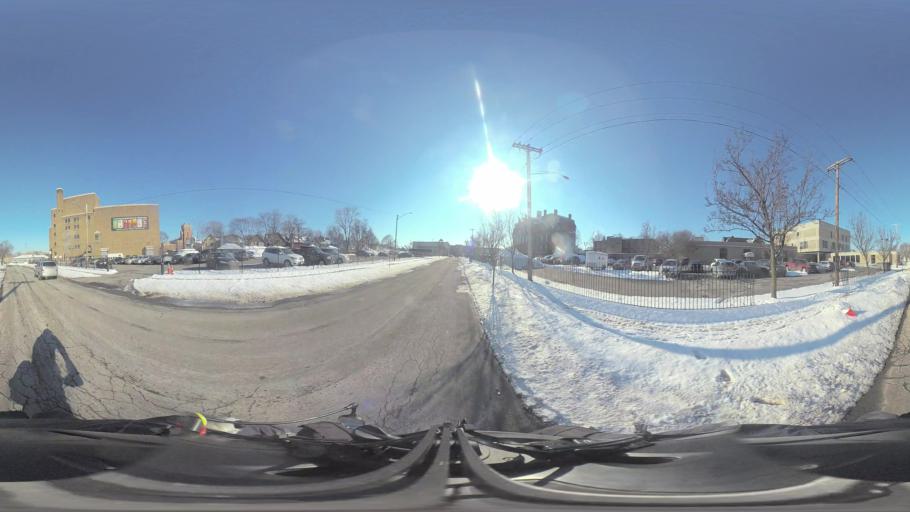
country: US
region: New York
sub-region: Monroe County
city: Rochester
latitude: 43.1597
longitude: -77.5881
